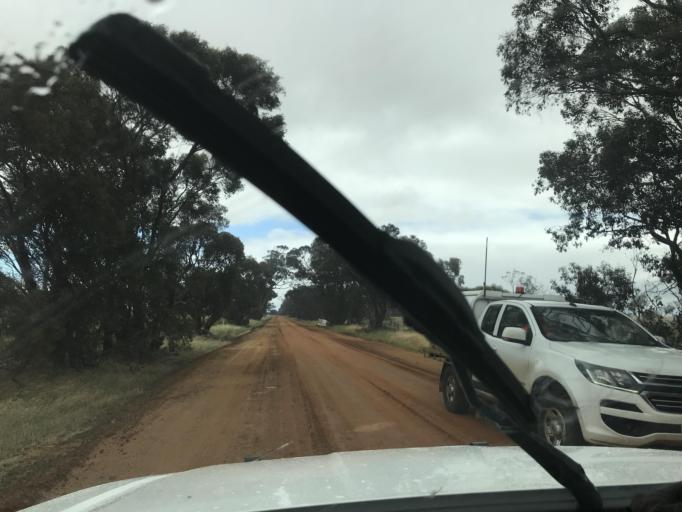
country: AU
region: South Australia
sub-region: Tatiara
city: Bordertown
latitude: -36.2660
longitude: 141.1509
